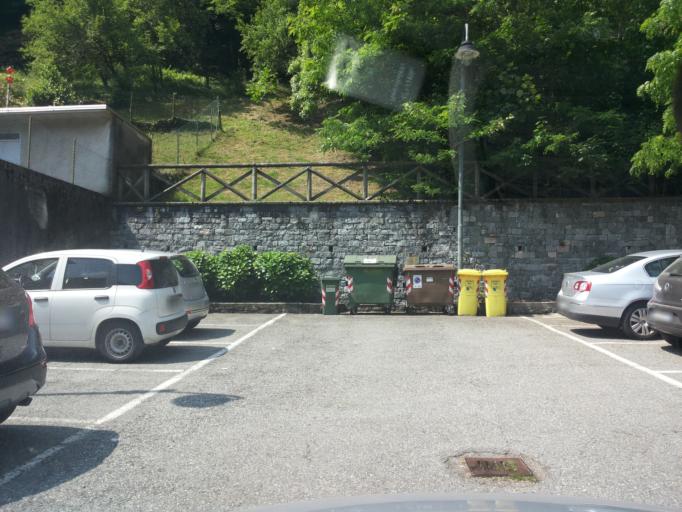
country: IT
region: Piedmont
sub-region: Provincia di Biella
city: Coggiola
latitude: 45.6929
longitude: 8.1699
